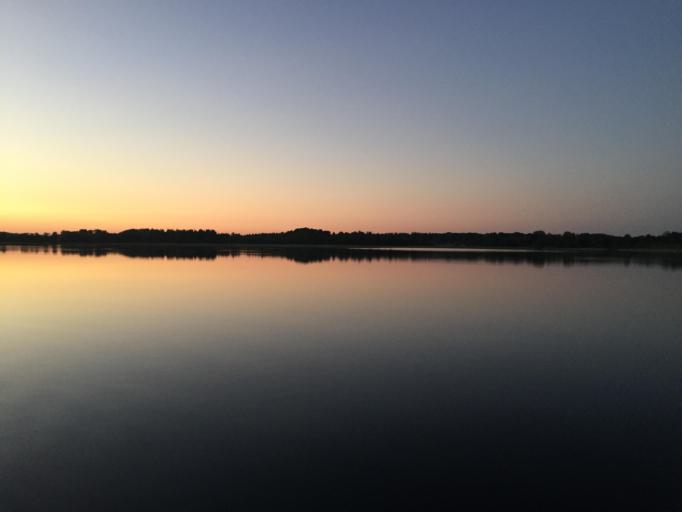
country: LV
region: Rezekne
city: Rezekne
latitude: 56.3613
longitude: 27.4250
